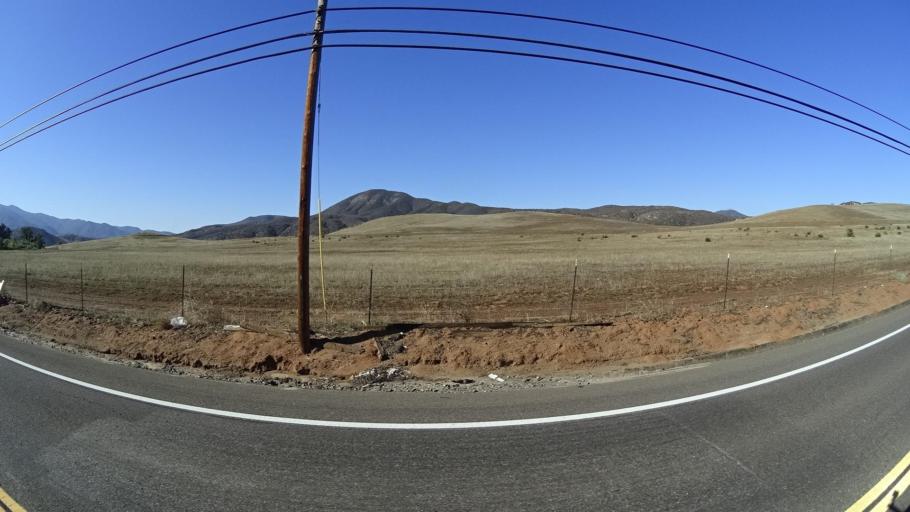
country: US
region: California
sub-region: San Diego County
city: Jamul
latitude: 32.6985
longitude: -116.8623
